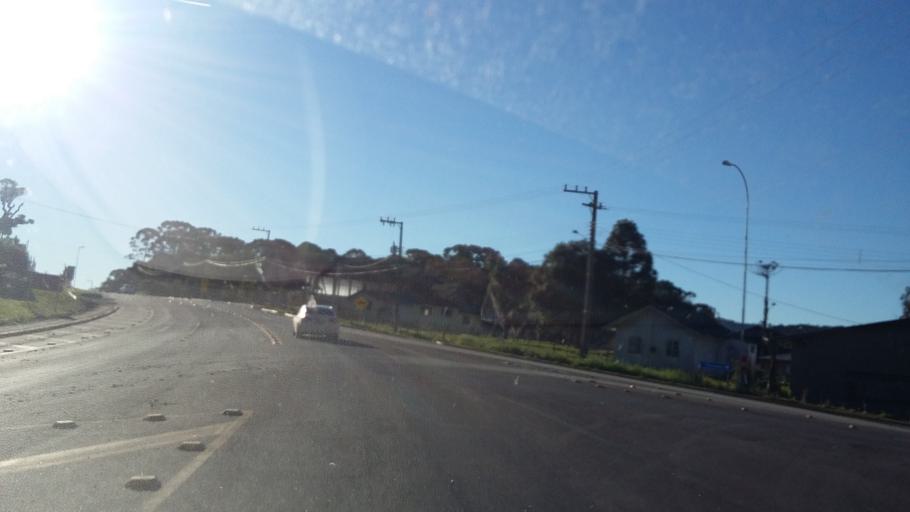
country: BR
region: Santa Catarina
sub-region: Lauro Muller
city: Lauro Muller
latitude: -28.0013
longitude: -49.5477
